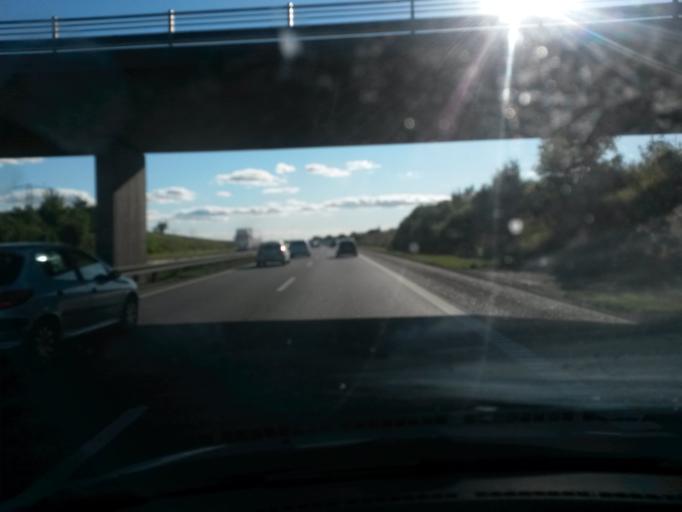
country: DK
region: Central Jutland
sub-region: Favrskov Kommune
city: Soften
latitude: 56.2110
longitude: 10.0904
